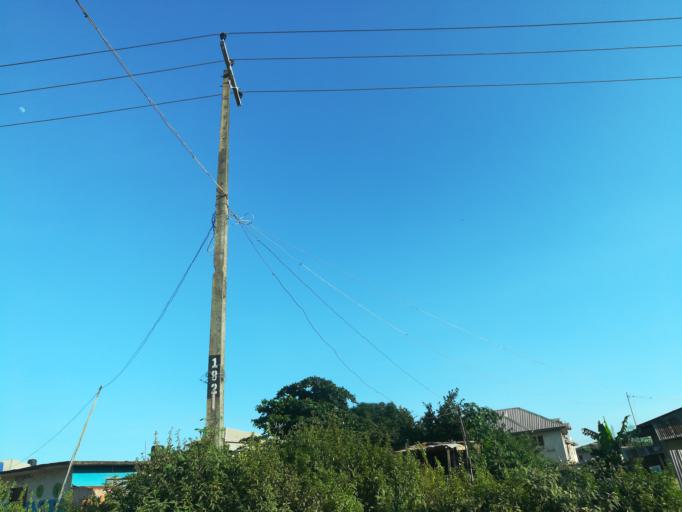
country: NG
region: Lagos
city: Ikorodu
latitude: 6.5915
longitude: 3.5135
